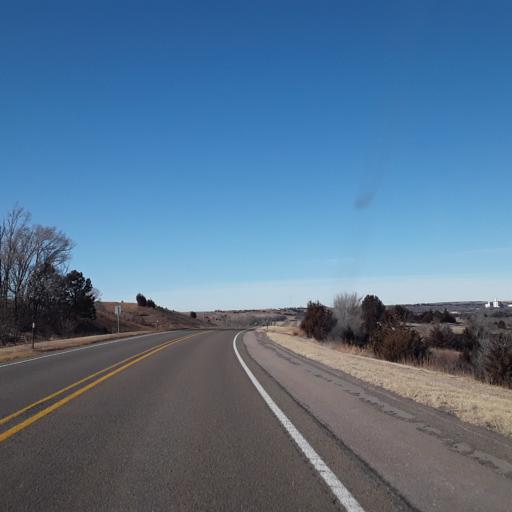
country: US
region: Nebraska
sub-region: Frontier County
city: Stockville
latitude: 40.6324
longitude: -100.5864
